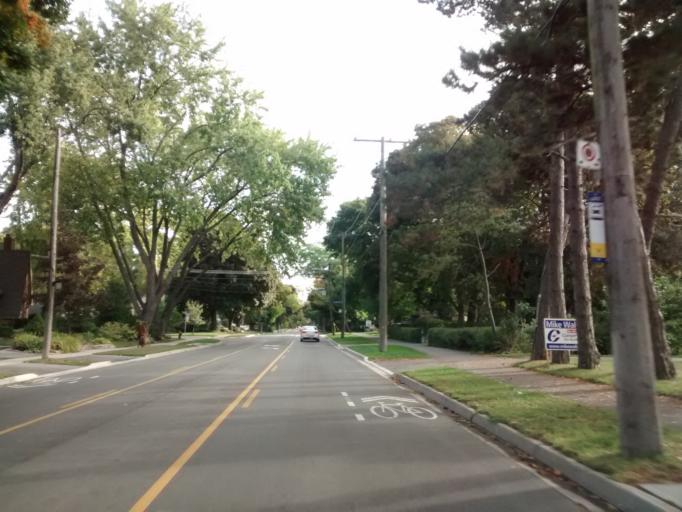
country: CA
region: Ontario
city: Burlington
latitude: 43.3304
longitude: -79.7839
